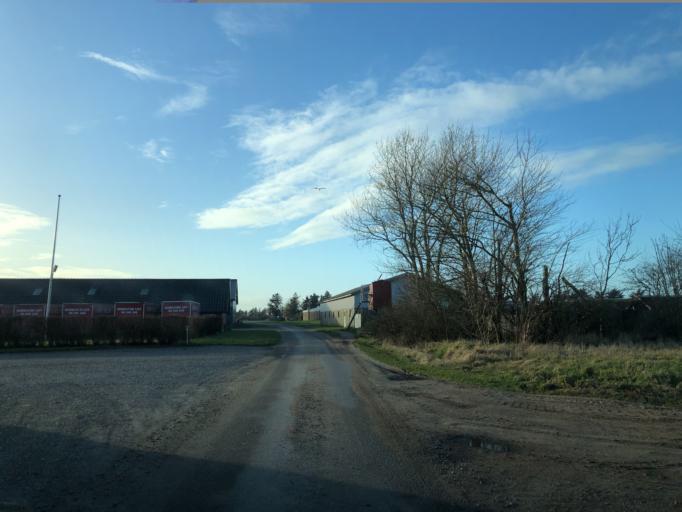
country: DK
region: Central Jutland
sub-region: Holstebro Kommune
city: Ulfborg
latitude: 56.3105
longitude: 8.2195
